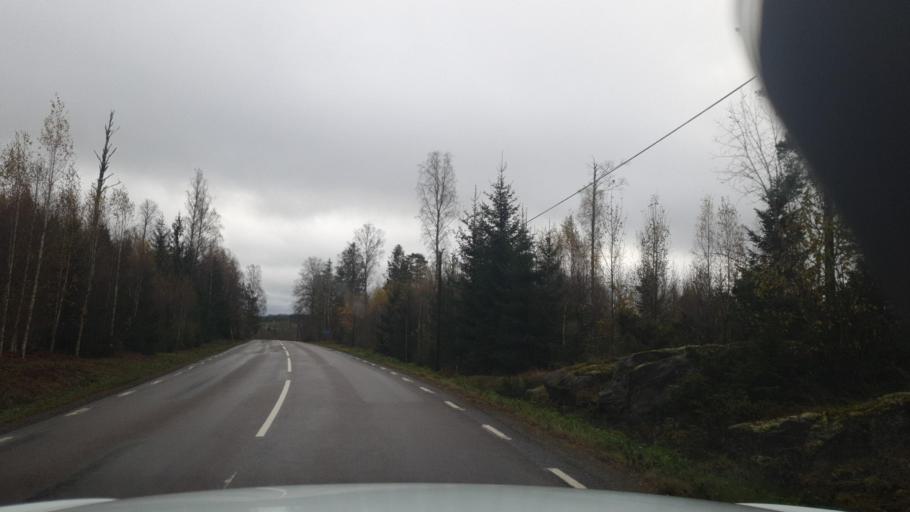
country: SE
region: Vaermland
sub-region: Eda Kommun
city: Amotfors
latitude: 59.7762
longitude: 12.2688
